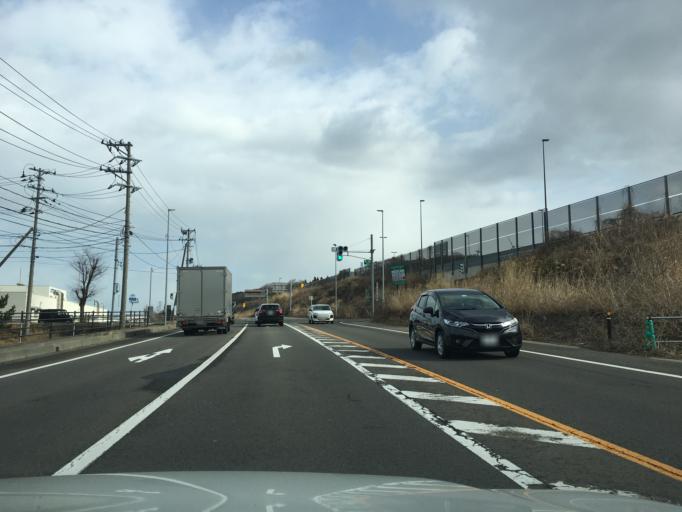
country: JP
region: Yamagata
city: Yuza
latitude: 39.2921
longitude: 139.9747
